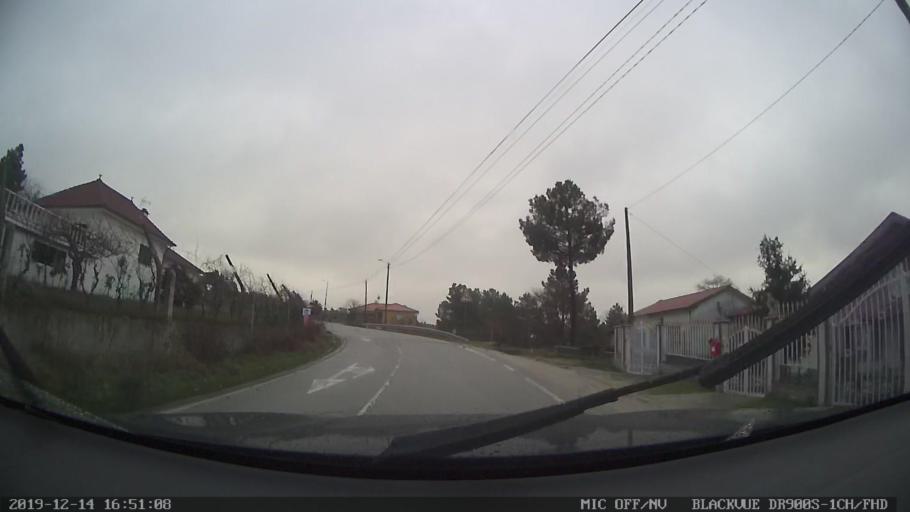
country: PT
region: Vila Real
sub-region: Murca
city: Murca
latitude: 41.4215
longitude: -7.5048
